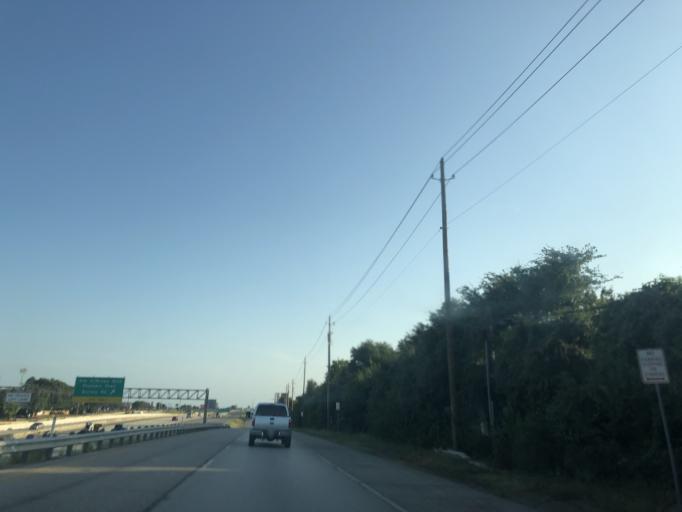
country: US
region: Texas
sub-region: Tarrant County
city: Arlington
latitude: 32.7682
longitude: -97.0626
